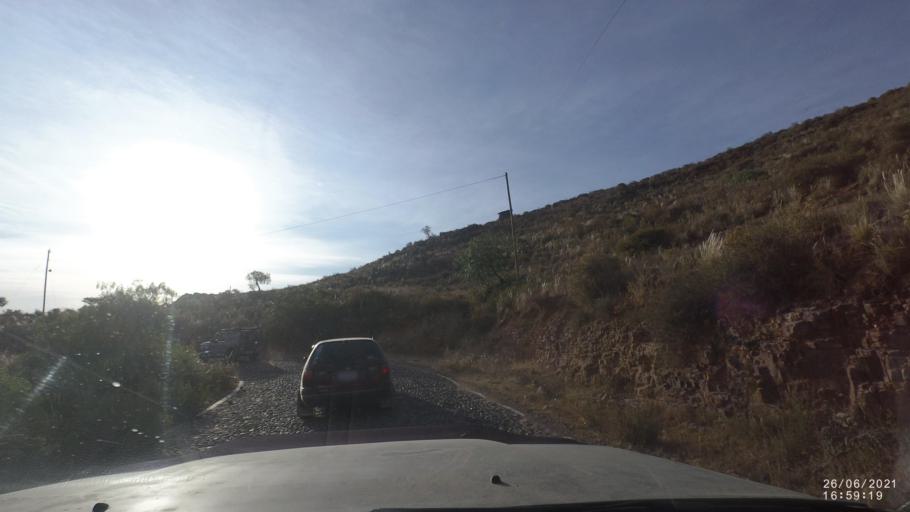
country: BO
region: Cochabamba
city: Cliza
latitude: -17.6663
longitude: -65.9077
